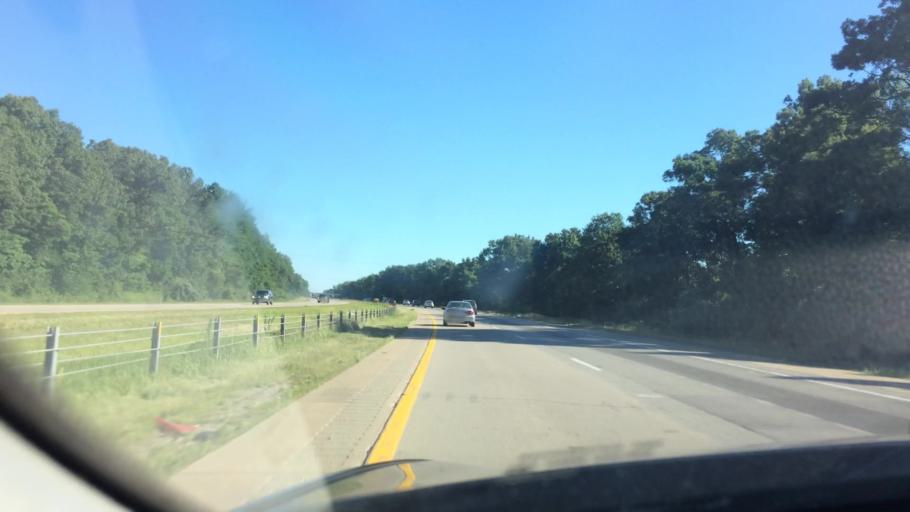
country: US
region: Michigan
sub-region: Monroe County
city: Petersburg
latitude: 41.8555
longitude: -83.6610
